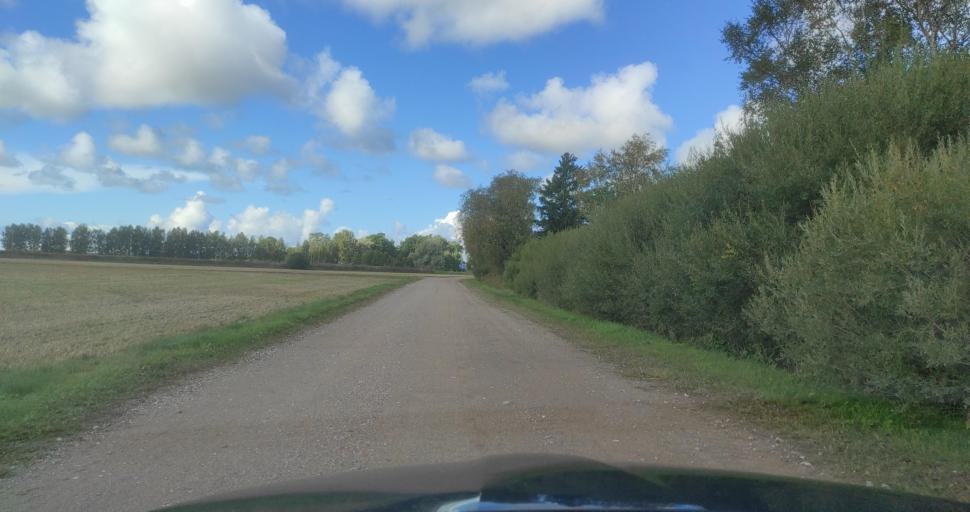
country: LV
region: Ventspils Rajons
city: Piltene
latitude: 57.2709
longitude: 21.5870
